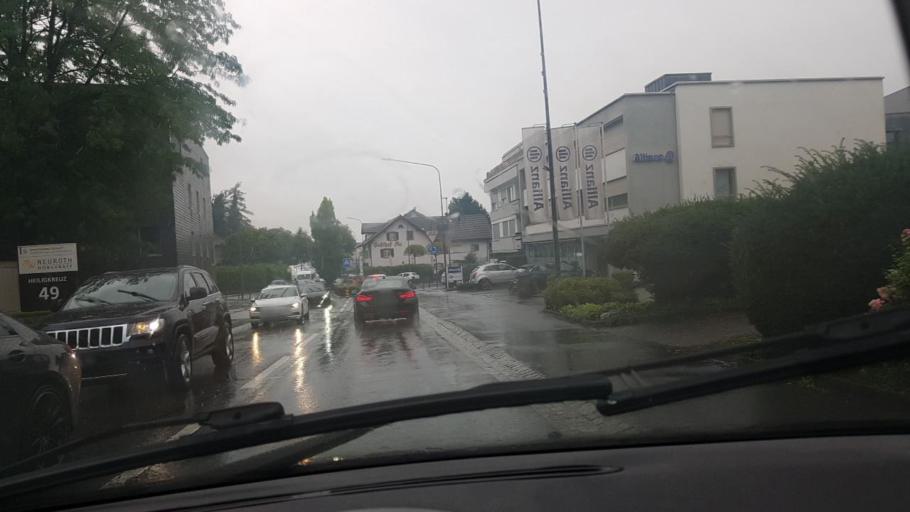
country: LI
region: Vaduz
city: Vaduz
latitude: 47.1334
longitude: 9.5221
